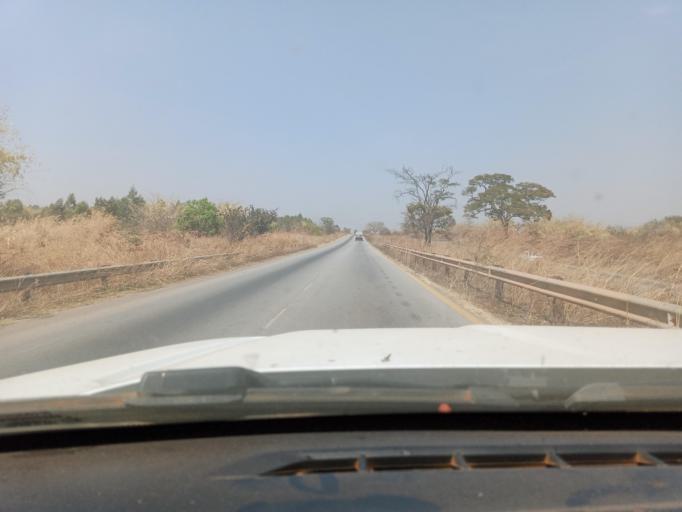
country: ZM
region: Copperbelt
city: Luanshya
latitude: -12.9909
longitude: 28.4159
